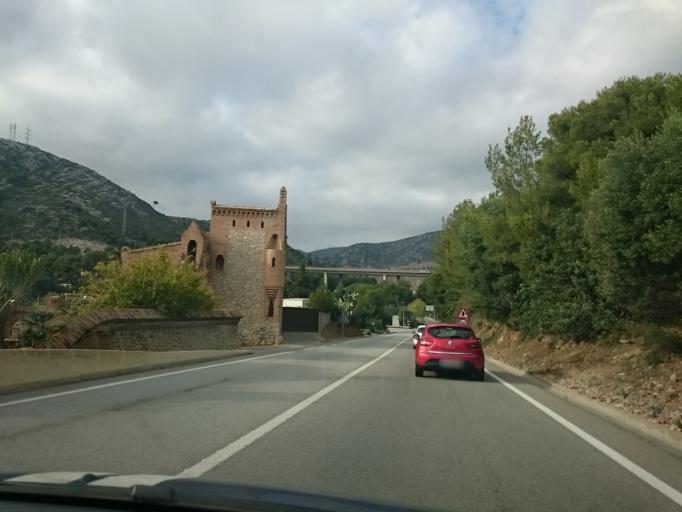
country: ES
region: Catalonia
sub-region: Provincia de Barcelona
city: Castelldefels
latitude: 41.2562
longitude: 1.9057
